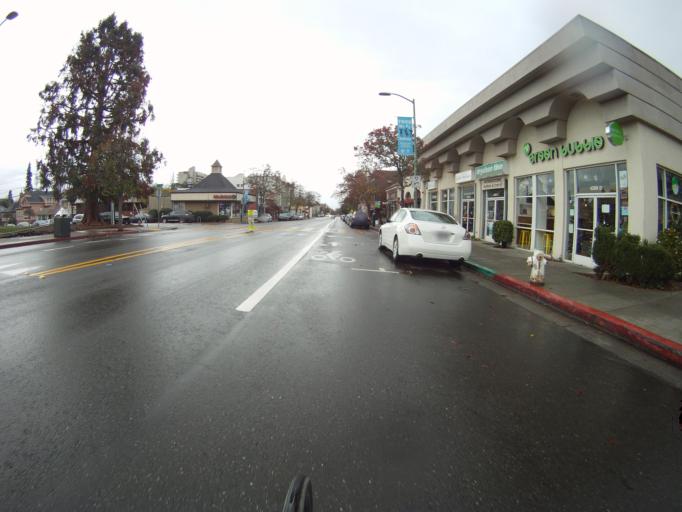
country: US
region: California
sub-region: Alameda County
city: Piedmont
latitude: 37.8288
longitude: -122.2496
